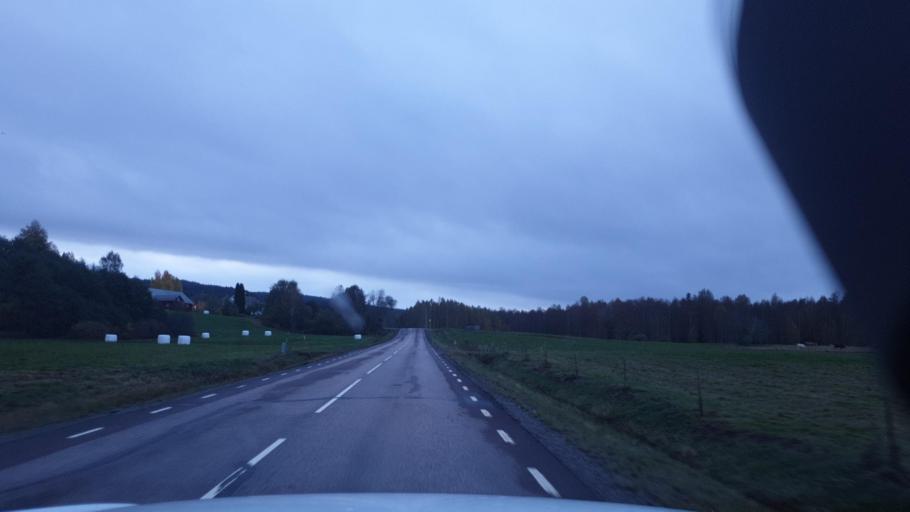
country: SE
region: Vaermland
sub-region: Arvika Kommun
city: Arvika
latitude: 59.7541
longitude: 12.6325
